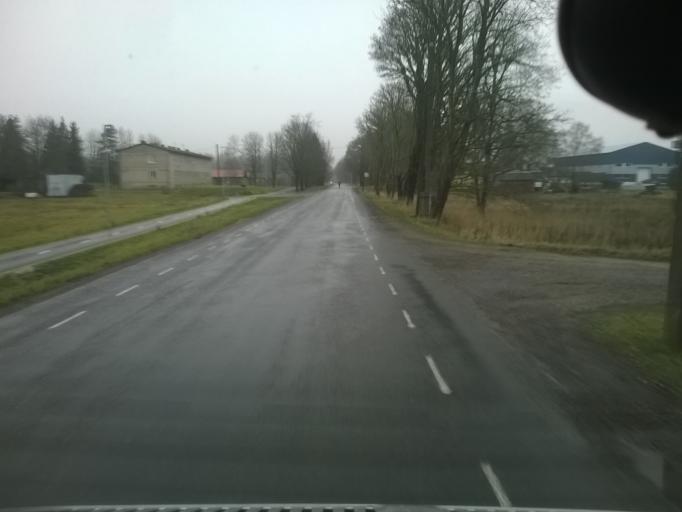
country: EE
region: Raplamaa
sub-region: Kohila vald
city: Kohila
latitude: 59.1604
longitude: 24.6504
